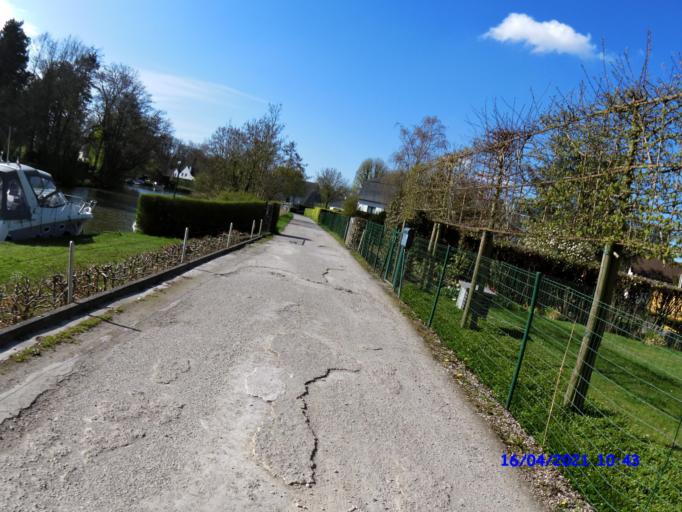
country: BE
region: Flanders
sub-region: Provincie Oost-Vlaanderen
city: Gent
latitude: 51.0318
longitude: 3.6785
